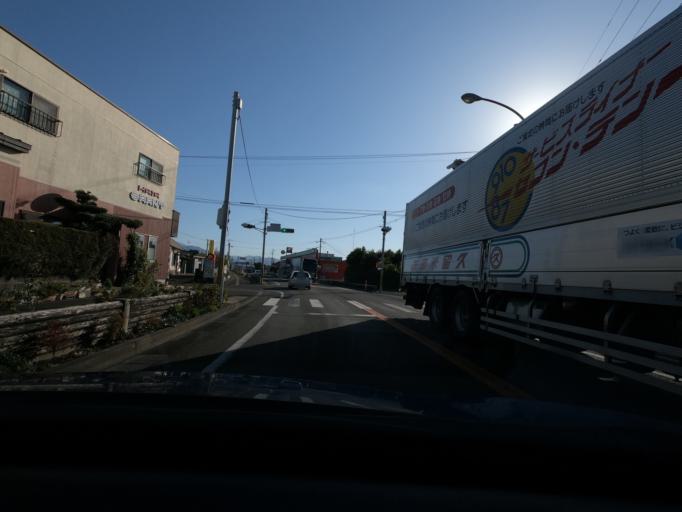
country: JP
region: Kagoshima
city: Izumi
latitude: 32.1205
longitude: 130.3400
